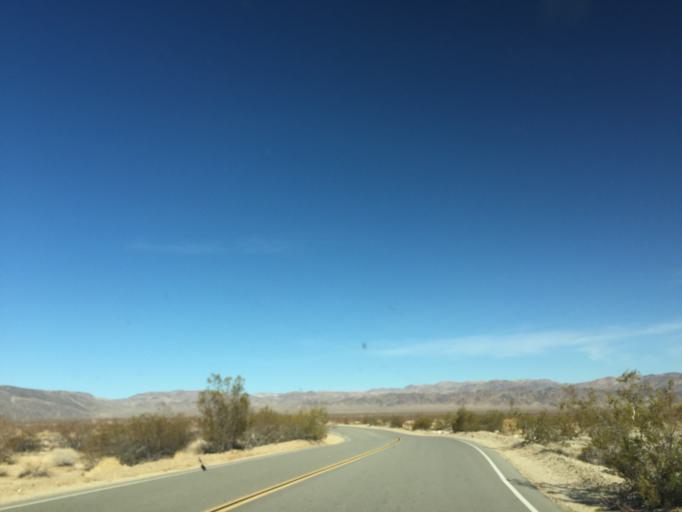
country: US
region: California
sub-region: San Bernardino County
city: Twentynine Palms
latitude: 33.9016
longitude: -115.8361
